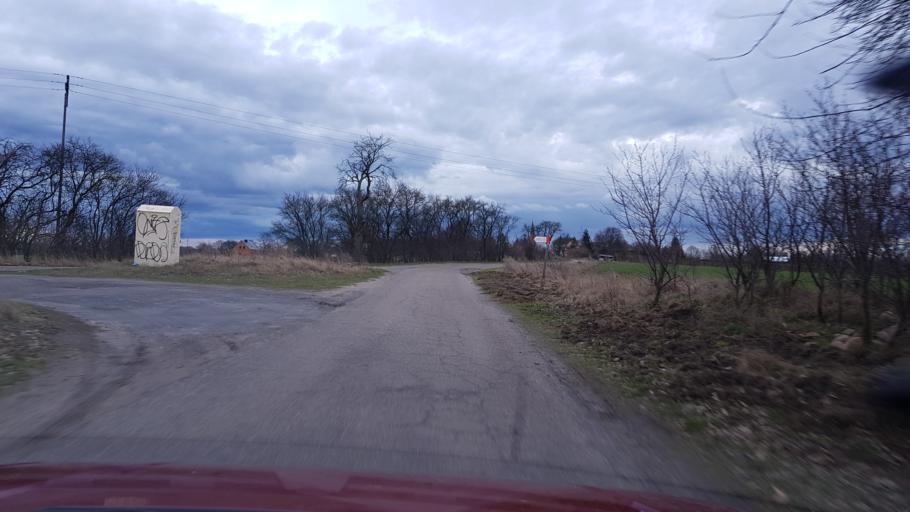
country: PL
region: West Pomeranian Voivodeship
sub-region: Powiat gryfinski
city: Stare Czarnowo
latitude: 53.3288
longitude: 14.6751
